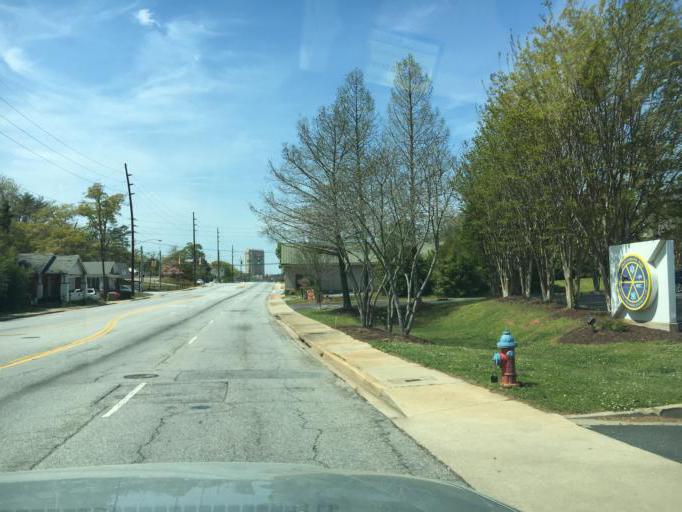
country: US
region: South Carolina
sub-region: Spartanburg County
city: Spartanburg
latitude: 34.9434
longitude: -81.9154
